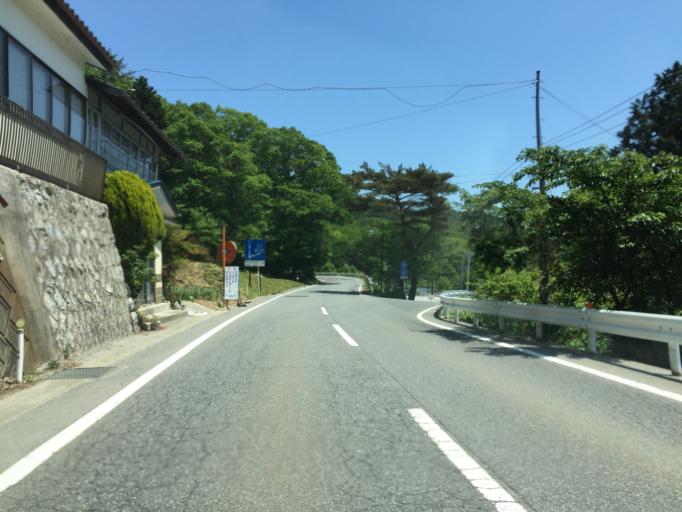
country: JP
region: Fukushima
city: Funehikimachi-funehiki
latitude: 37.5030
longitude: 140.7714
